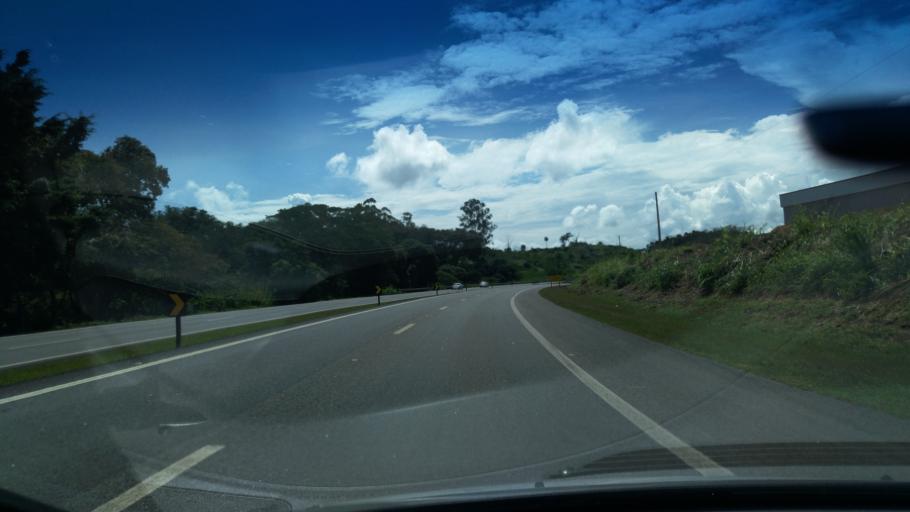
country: BR
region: Sao Paulo
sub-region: Santo Antonio Do Jardim
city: Espirito Santo do Pinhal
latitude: -22.2235
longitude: -46.7927
